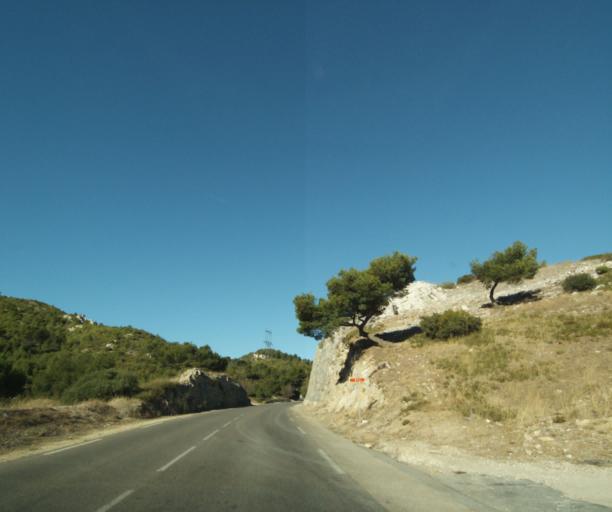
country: FR
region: Provence-Alpes-Cote d'Azur
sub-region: Departement des Bouches-du-Rhone
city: Le Rove
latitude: 43.3608
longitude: 5.2718
